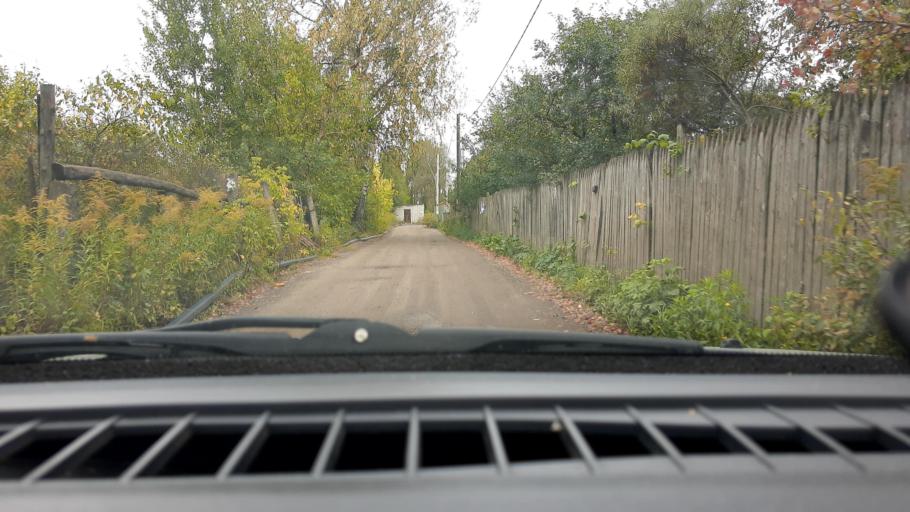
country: RU
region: Nizjnij Novgorod
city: Gorbatovka
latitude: 56.3231
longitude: 43.8387
